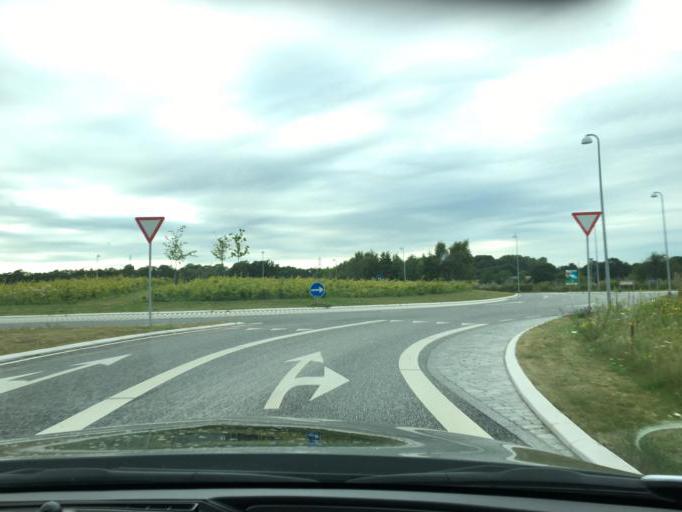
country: DK
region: Capital Region
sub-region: Allerod Kommune
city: Blovstrod
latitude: 55.9079
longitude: 12.4021
